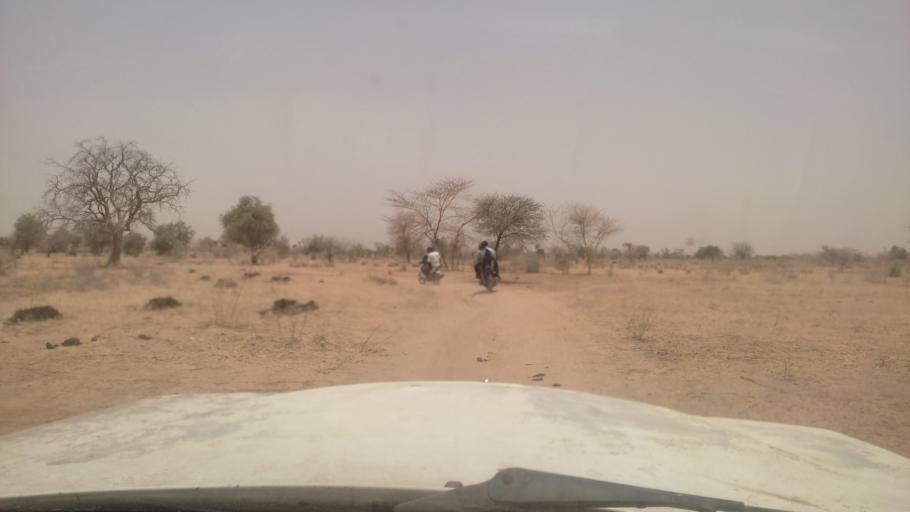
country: BF
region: Est
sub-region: Gnagna Province
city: Bogande
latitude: 13.0307
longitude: -0.0755
